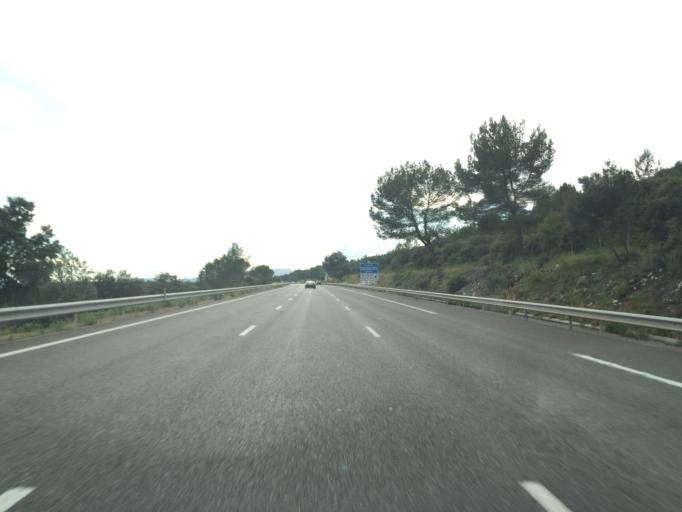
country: FR
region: Provence-Alpes-Cote d'Azur
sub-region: Departement du Var
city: La Celle
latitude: 43.4215
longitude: 6.0106
